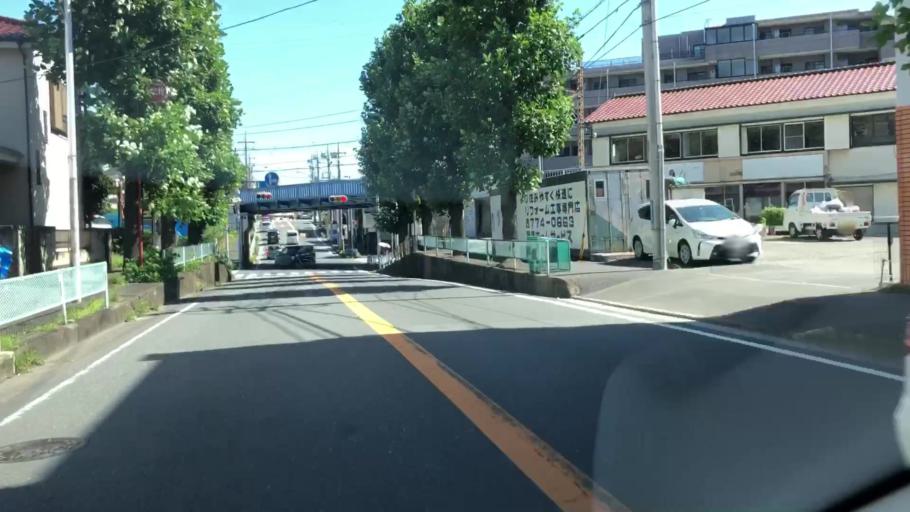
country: JP
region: Kanagawa
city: Yokohama
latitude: 35.3790
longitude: 139.6078
